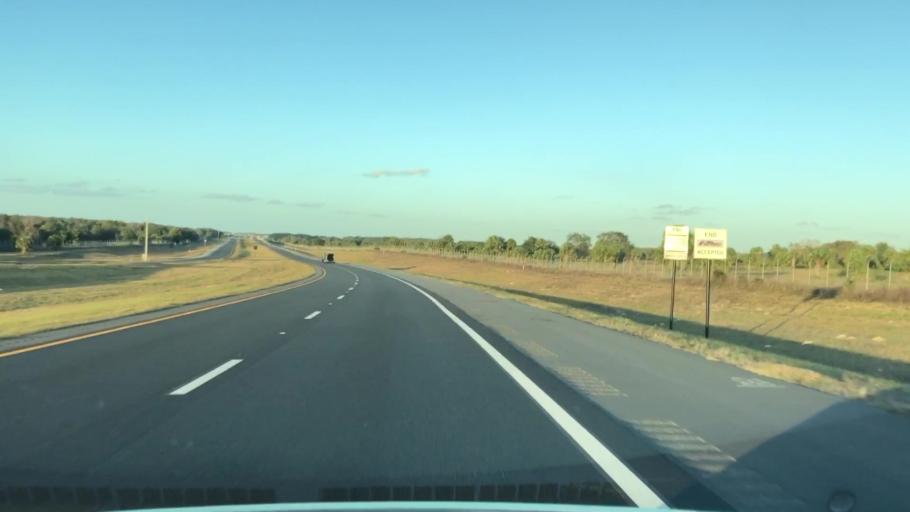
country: US
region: Florida
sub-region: Lake County
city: Mount Plymouth
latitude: 28.7815
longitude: -81.5220
